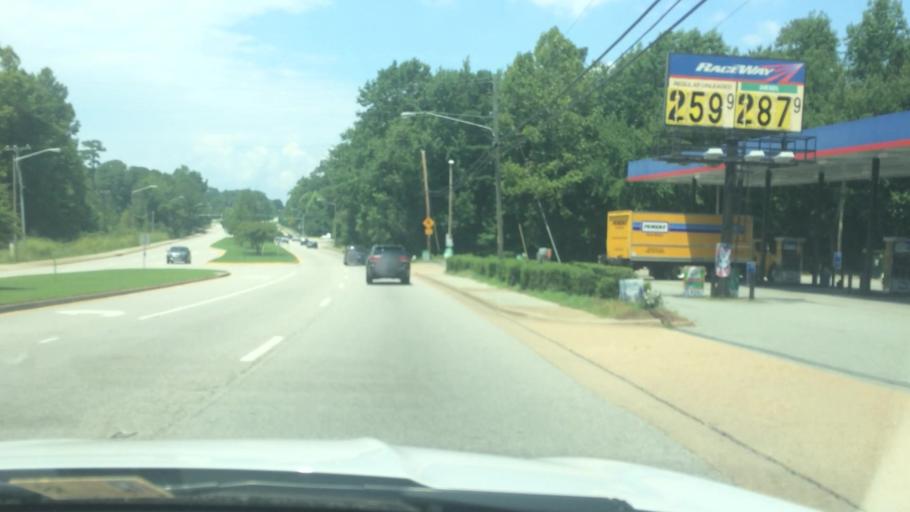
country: US
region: Virginia
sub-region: York County
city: Yorktown
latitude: 37.1661
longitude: -76.5584
